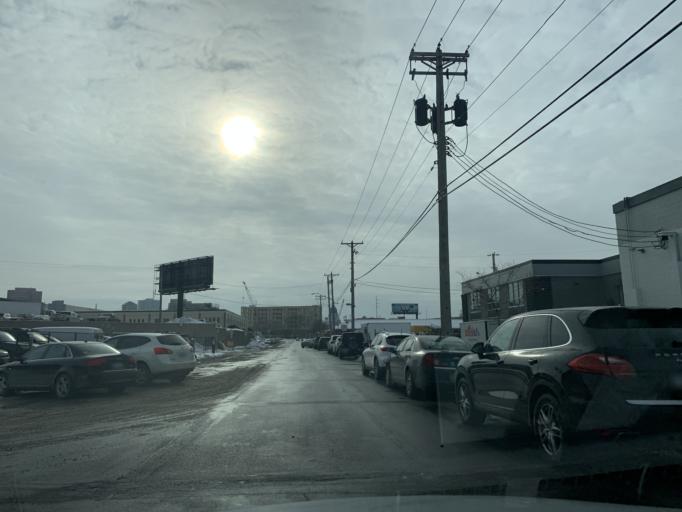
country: US
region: Minnesota
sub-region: Hennepin County
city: Minneapolis
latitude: 44.9827
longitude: -93.2853
